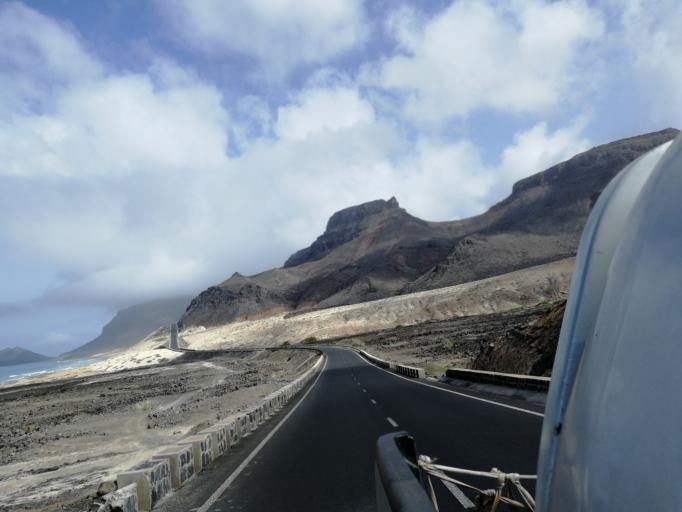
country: CV
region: Sao Vicente
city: Mindelo
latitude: 16.8747
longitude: -24.9095
